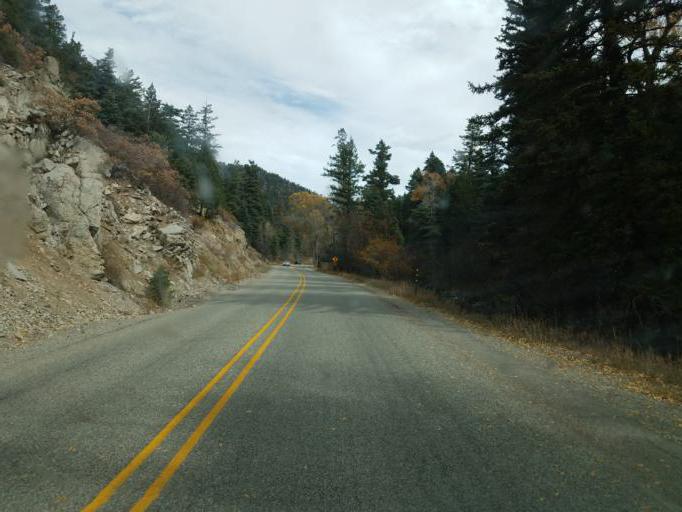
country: US
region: New Mexico
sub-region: Taos County
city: Arroyo Seco
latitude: 36.5524
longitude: -105.5402
